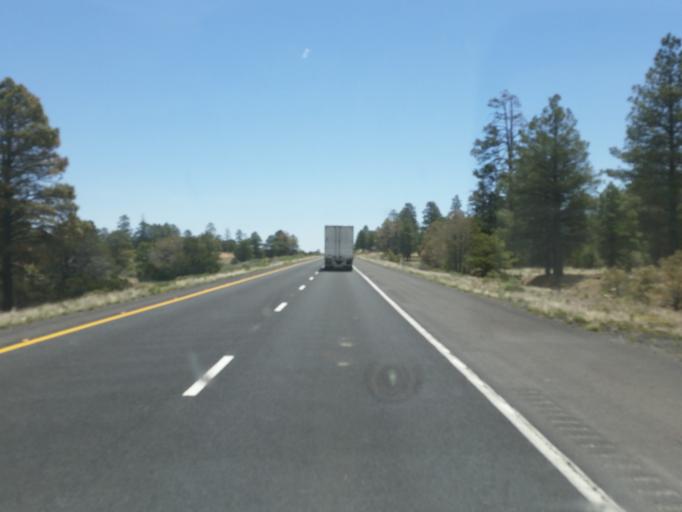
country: US
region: Arizona
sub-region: Coconino County
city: Flagstaff
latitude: 35.2132
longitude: -111.5378
